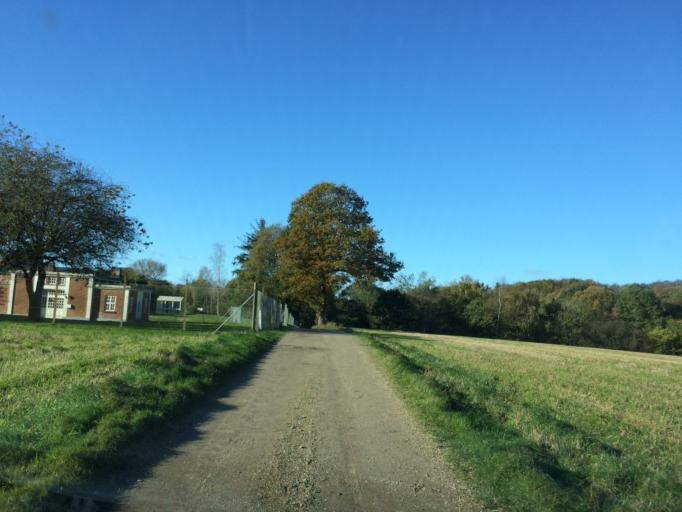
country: DK
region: South Denmark
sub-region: Fredericia Kommune
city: Taulov
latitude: 55.5686
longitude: 9.6355
